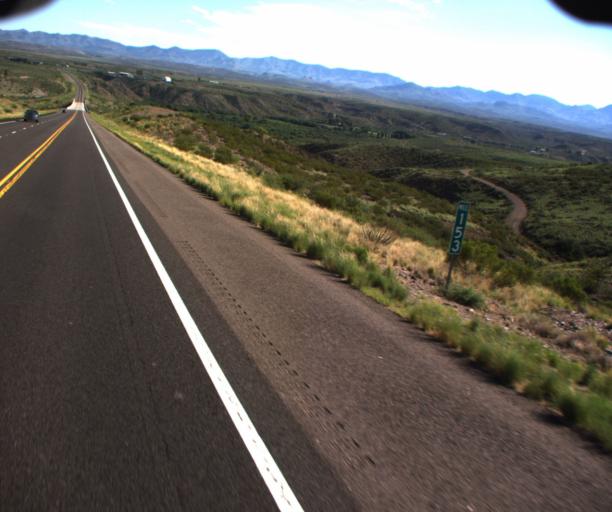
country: US
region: Arizona
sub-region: Greenlee County
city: Clifton
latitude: 32.9292
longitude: -109.2383
